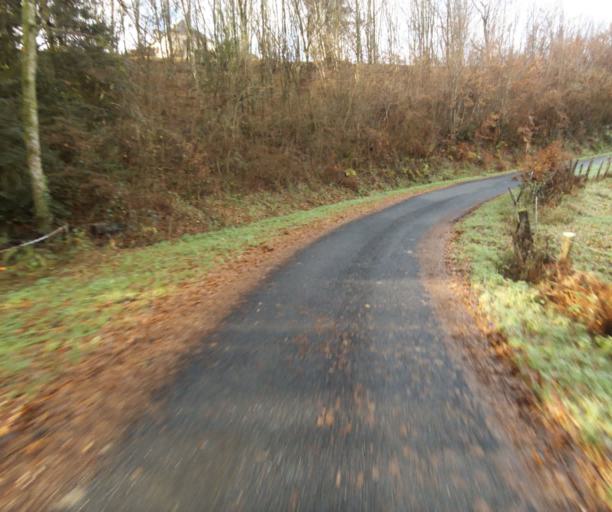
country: FR
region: Limousin
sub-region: Departement de la Correze
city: Saint-Mexant
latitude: 45.2547
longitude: 1.6173
